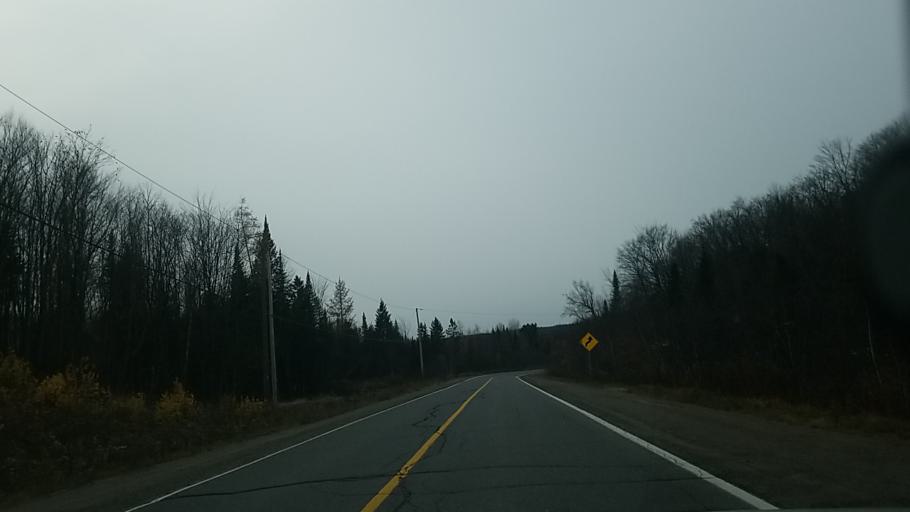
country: CA
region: Quebec
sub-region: Laurentides
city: Saint-Colomban
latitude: 45.7947
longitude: -74.1615
